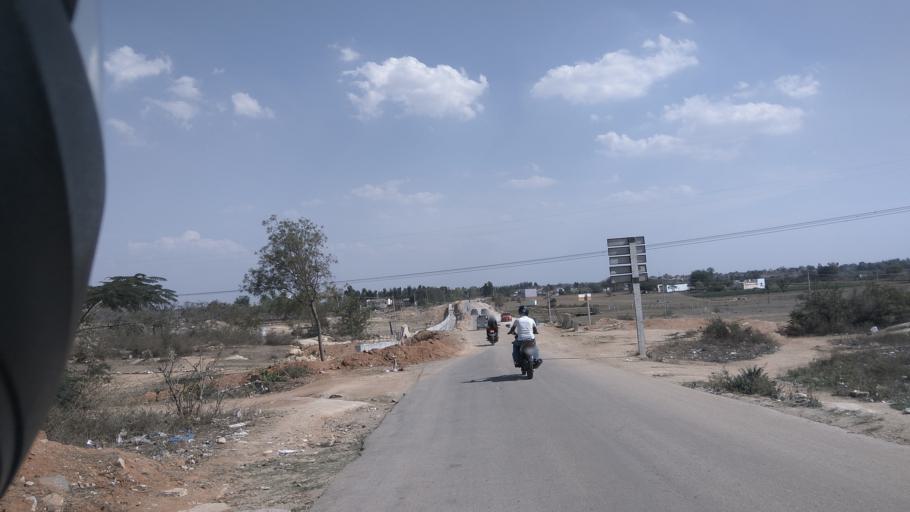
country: IN
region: Karnataka
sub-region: Kolar
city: Mulbagal
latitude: 13.1861
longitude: 78.3494
